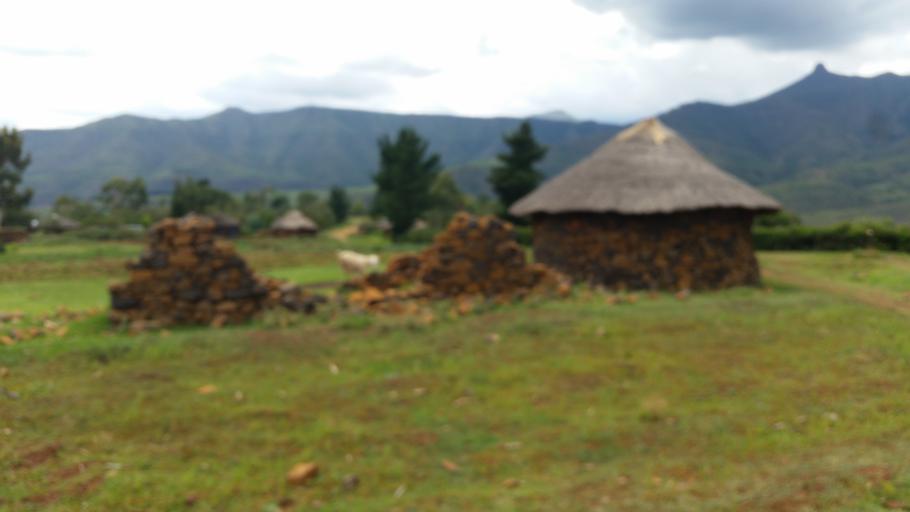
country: LS
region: Maseru
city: Nako
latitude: -29.5911
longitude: 27.7539
